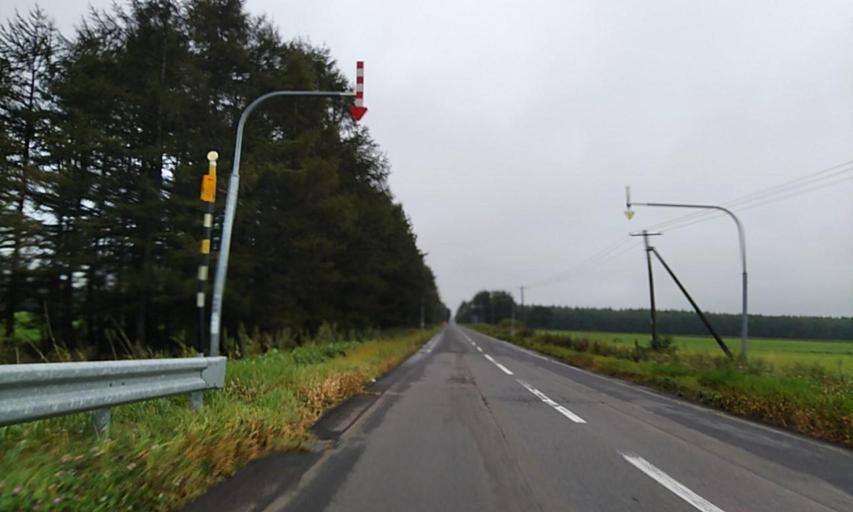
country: JP
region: Hokkaido
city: Shibetsu
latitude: 43.5048
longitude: 144.6616
